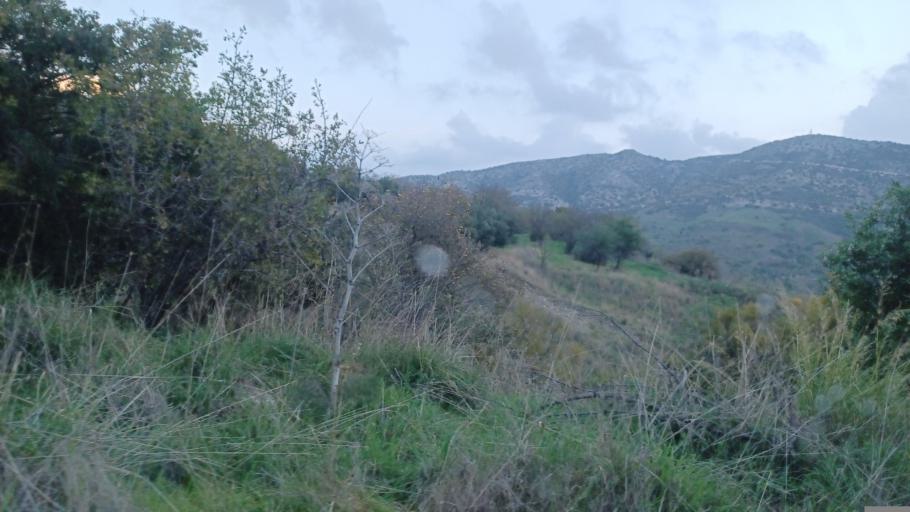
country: CY
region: Pafos
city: Mesogi
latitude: 34.7896
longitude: 32.5263
